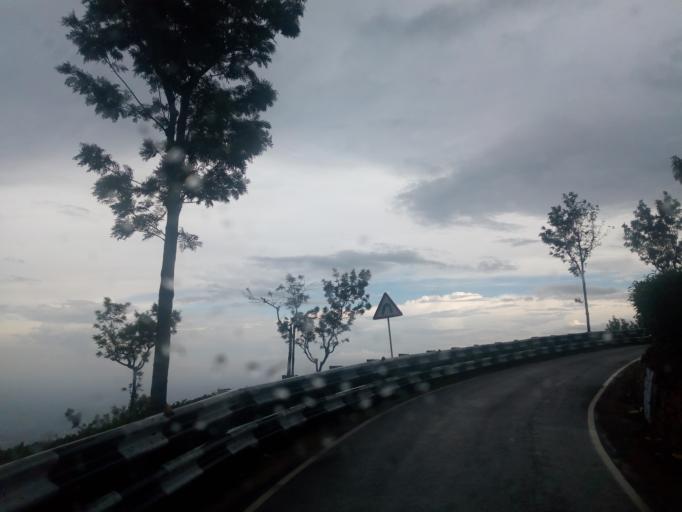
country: IN
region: Tamil Nadu
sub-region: Nilgiri
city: Kotagiri
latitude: 11.3665
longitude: 76.8562
